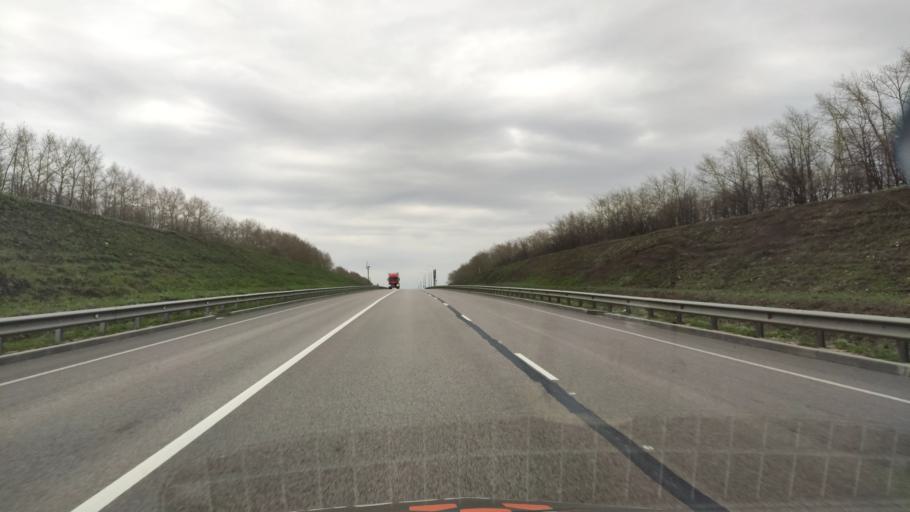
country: RU
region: Voronezj
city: Nizhnedevitsk
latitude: 51.5581
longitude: 38.2401
